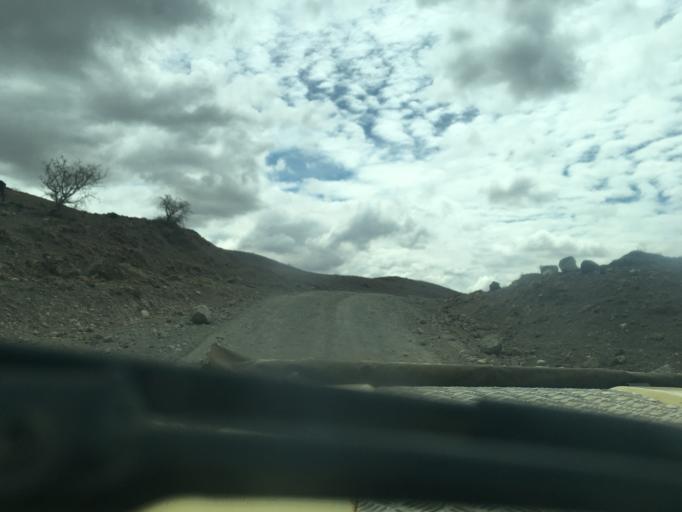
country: TZ
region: Arusha
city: Mto wa Mbu
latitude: -2.7654
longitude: 35.9847
